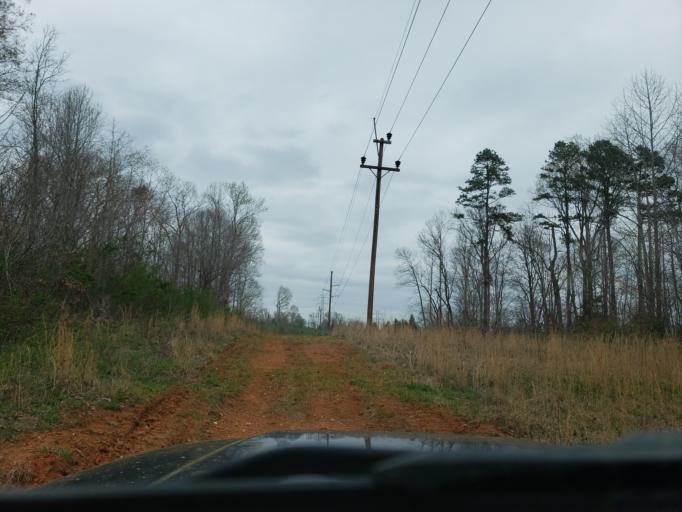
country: US
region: North Carolina
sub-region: Cleveland County
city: White Plains
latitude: 35.1881
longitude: -81.3701
